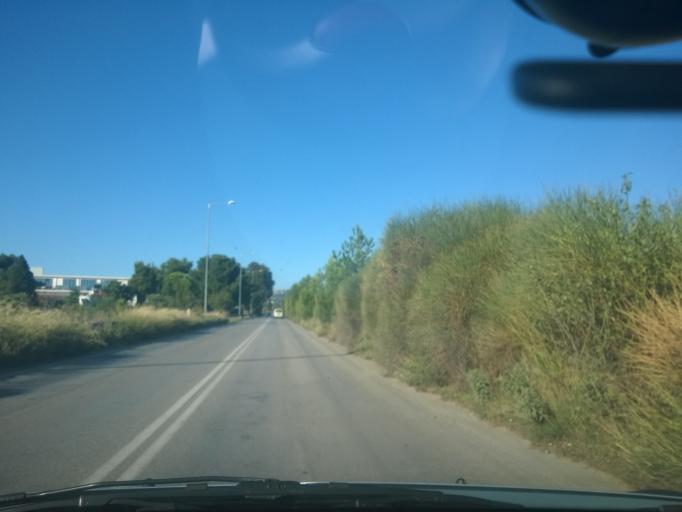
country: GR
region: Central Macedonia
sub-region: Nomos Thessalonikis
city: Thermi
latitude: 40.5344
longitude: 23.0146
